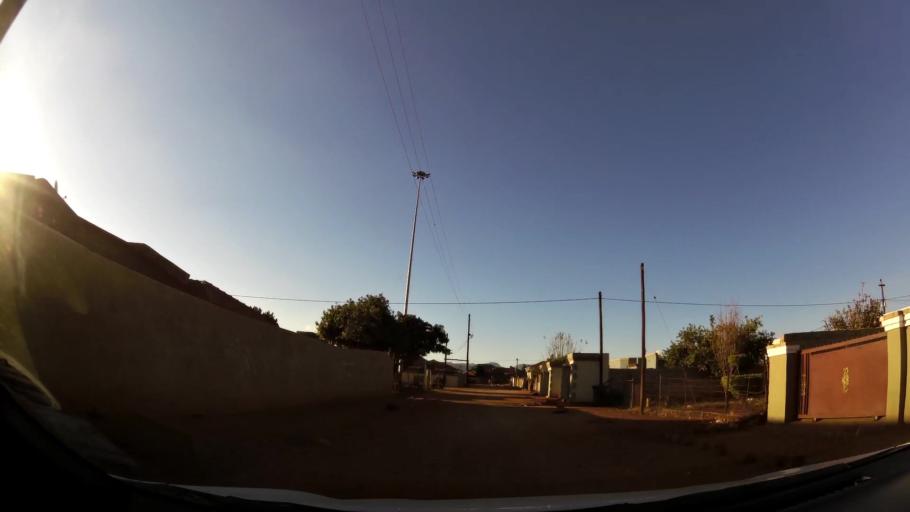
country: ZA
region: Limpopo
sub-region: Waterberg District Municipality
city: Mokopane
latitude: -24.1551
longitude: 28.9923
